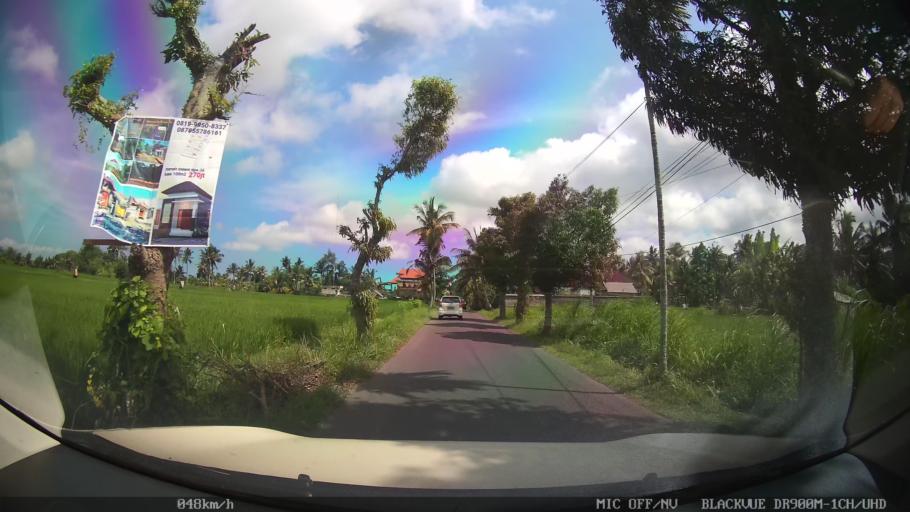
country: ID
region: Bali
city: Banjar Mulung
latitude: -8.5060
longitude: 115.3203
